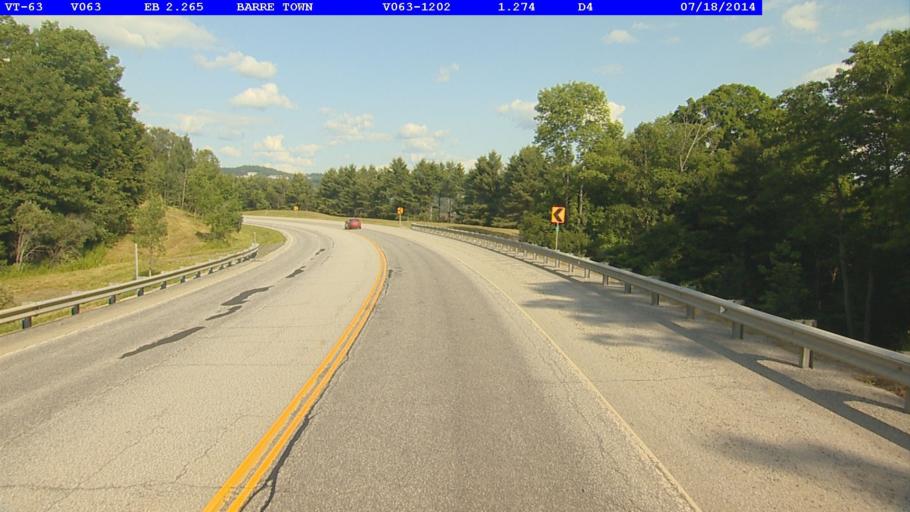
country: US
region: Vermont
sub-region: Washington County
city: South Barre
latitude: 44.1630
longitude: -72.5343
